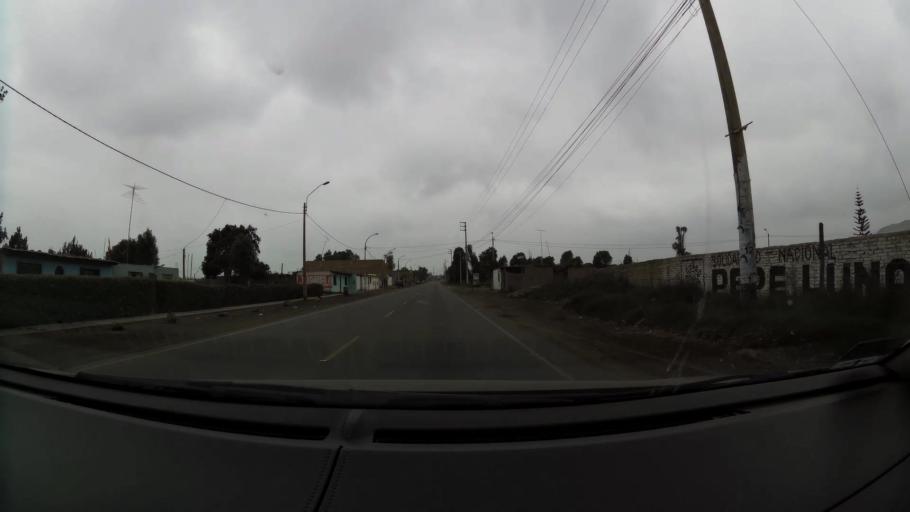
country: PE
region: Lima
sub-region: Provincia de Huaral
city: Huaral
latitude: -11.5223
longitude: -77.2452
